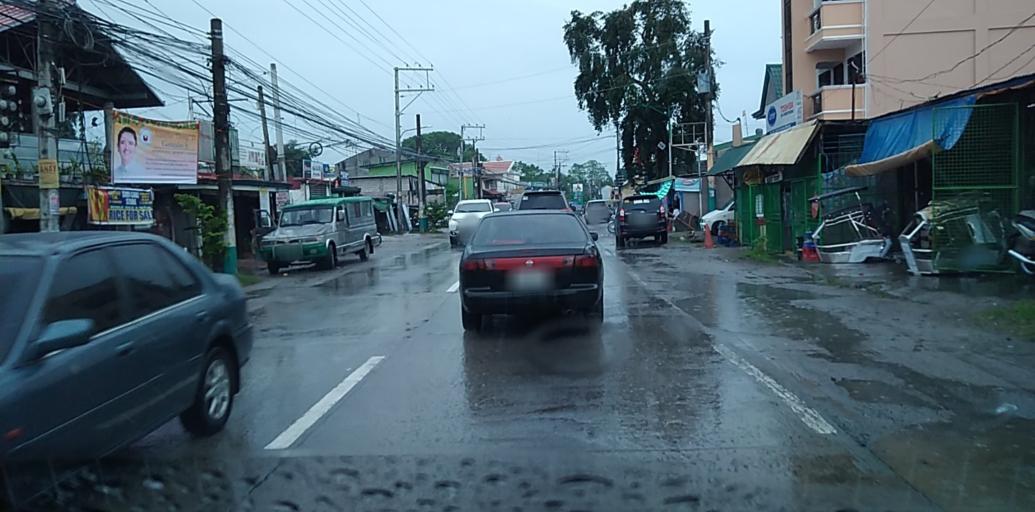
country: PH
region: Central Luzon
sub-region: Province of Pampanga
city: Mexico
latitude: 15.0597
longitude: 120.7190
